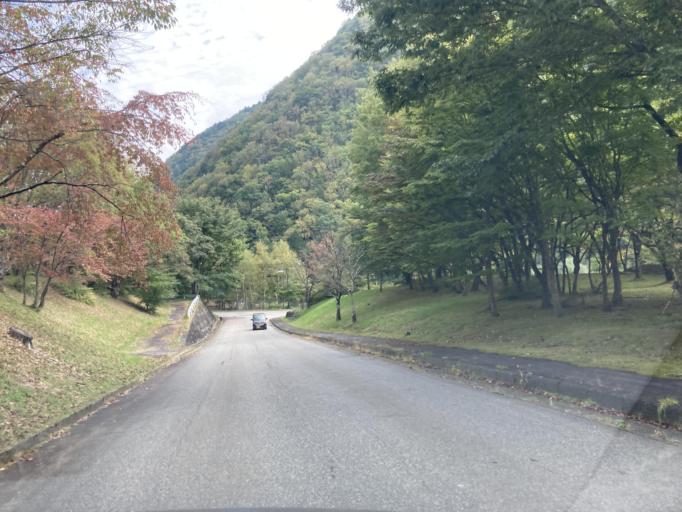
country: JP
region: Nagano
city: Omachi
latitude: 36.5151
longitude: 137.7836
